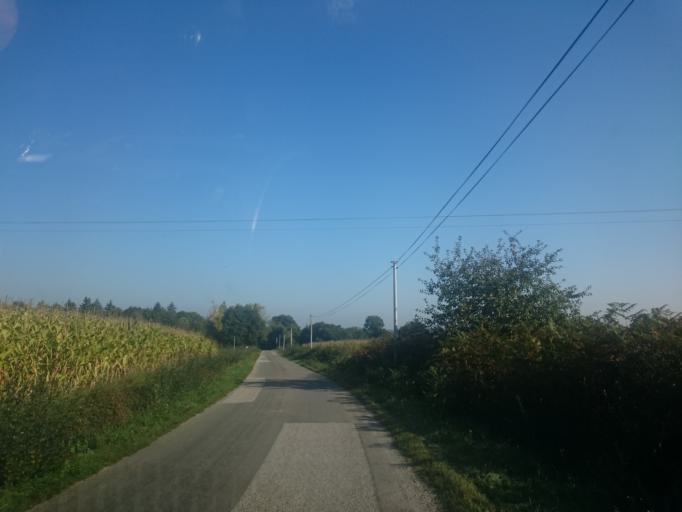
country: FR
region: Brittany
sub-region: Departement d'Ille-et-Vilaine
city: Tresboeuf
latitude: 47.9219
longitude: -1.5662
